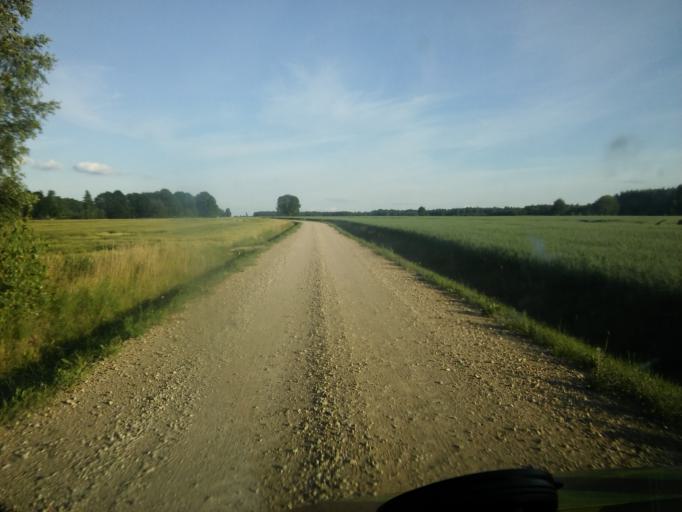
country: EE
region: Valgamaa
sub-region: Torva linn
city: Torva
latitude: 58.0710
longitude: 25.9025
